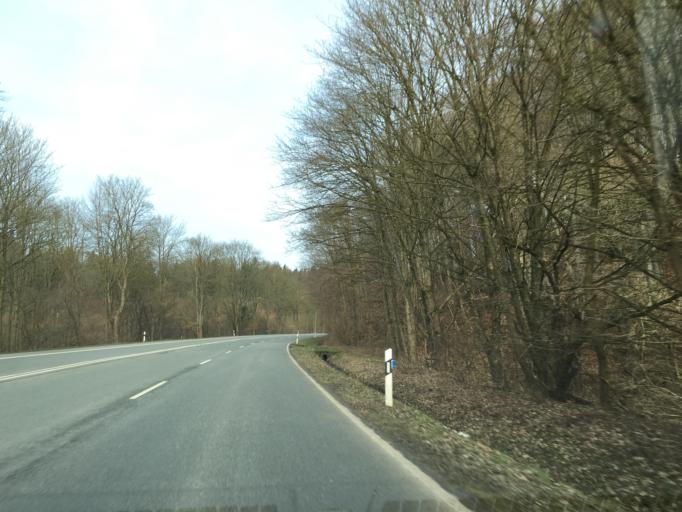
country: DE
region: North Rhine-Westphalia
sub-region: Regierungsbezirk Detmold
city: Willebadessen
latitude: 51.5457
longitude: 9.0115
